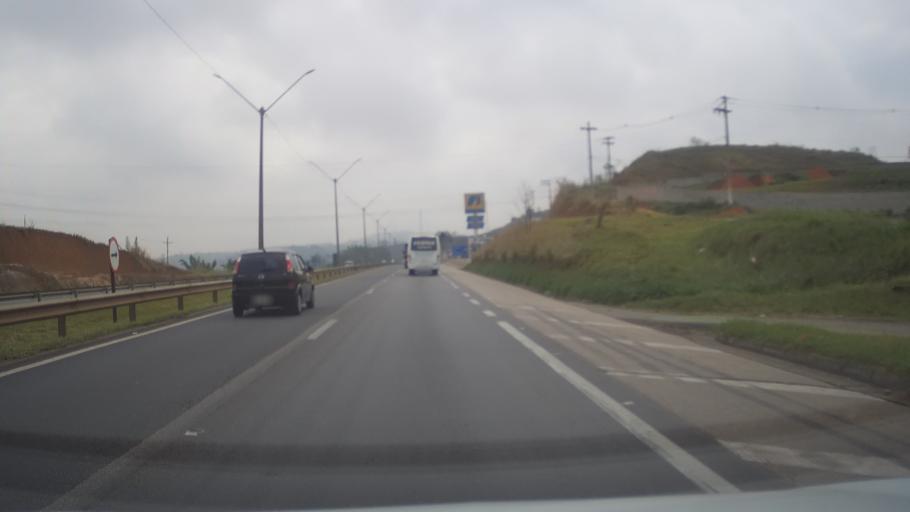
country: BR
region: Sao Paulo
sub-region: Atibaia
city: Atibaia
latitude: -23.0362
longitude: -46.5517
